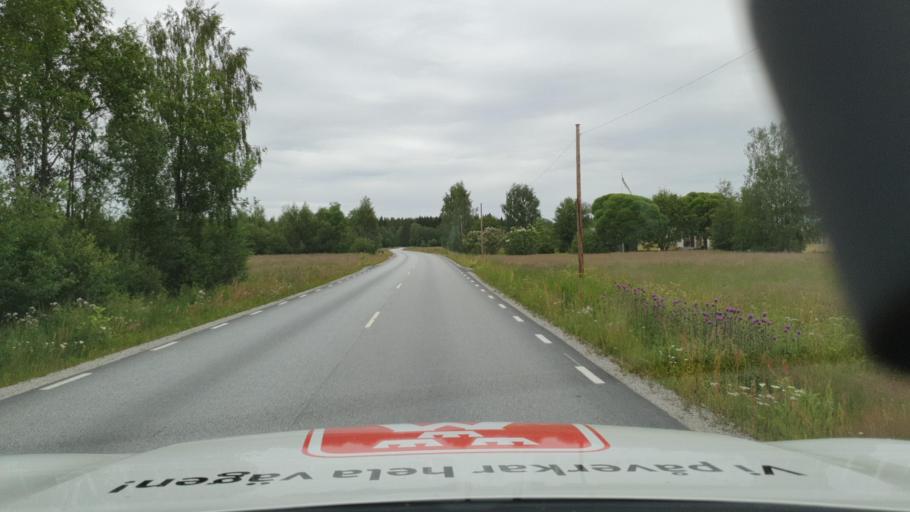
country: SE
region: Vaesterbotten
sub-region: Nordmalings Kommun
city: Nordmaling
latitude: 63.5635
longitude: 19.4133
